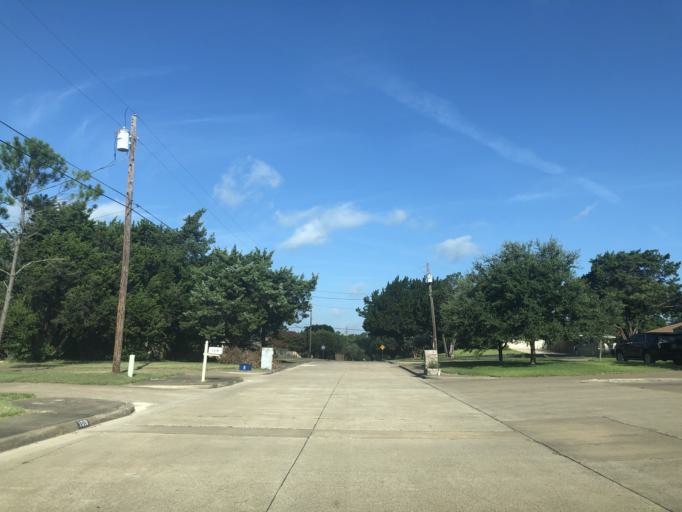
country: US
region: Texas
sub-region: Dallas County
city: Duncanville
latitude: 32.6571
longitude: -96.9310
